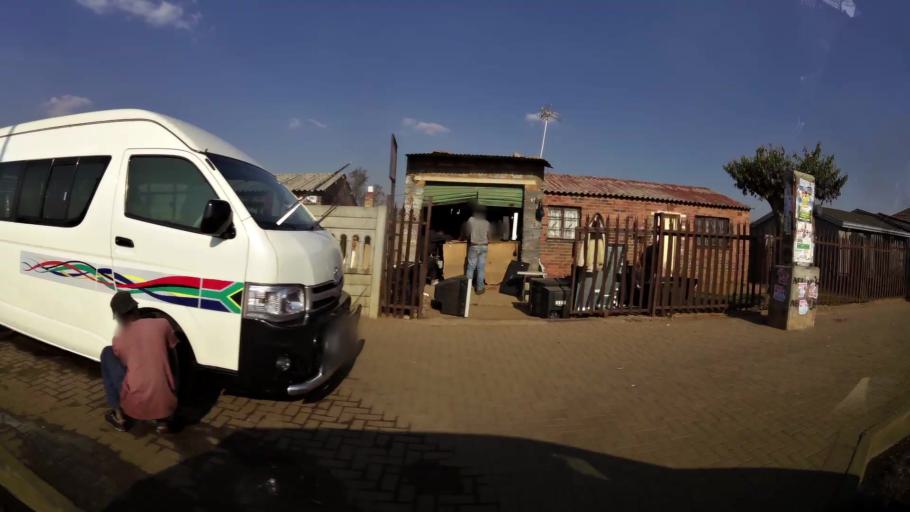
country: ZA
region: Gauteng
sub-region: Ekurhuleni Metropolitan Municipality
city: Brakpan
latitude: -26.1445
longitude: 28.4230
